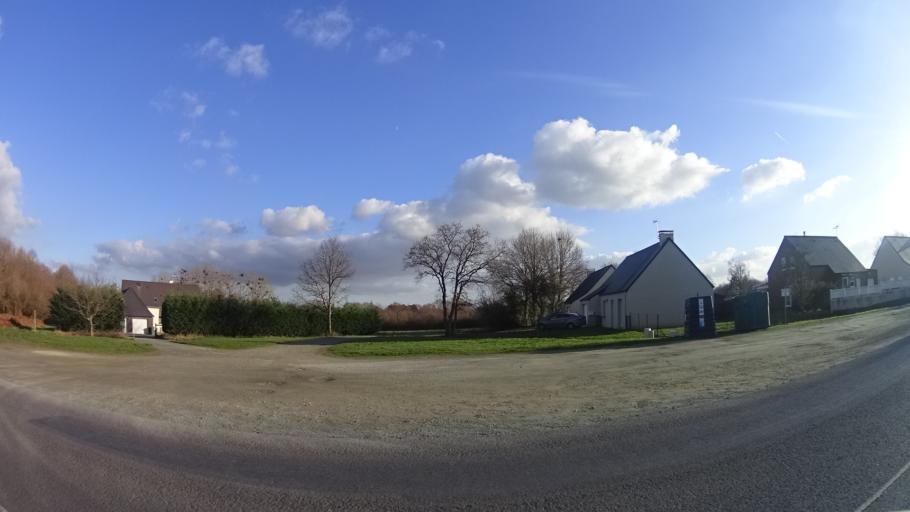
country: FR
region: Pays de la Loire
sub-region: Departement de la Loire-Atlantique
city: Plesse
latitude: 47.5466
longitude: -1.8773
